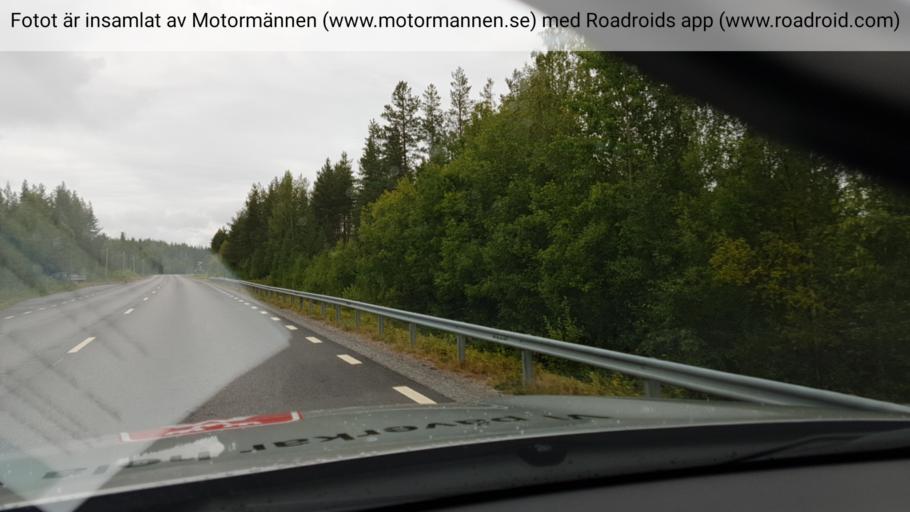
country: SE
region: Norrbotten
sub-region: Alvsbyns Kommun
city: AElvsbyn
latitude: 66.3002
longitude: 20.8080
